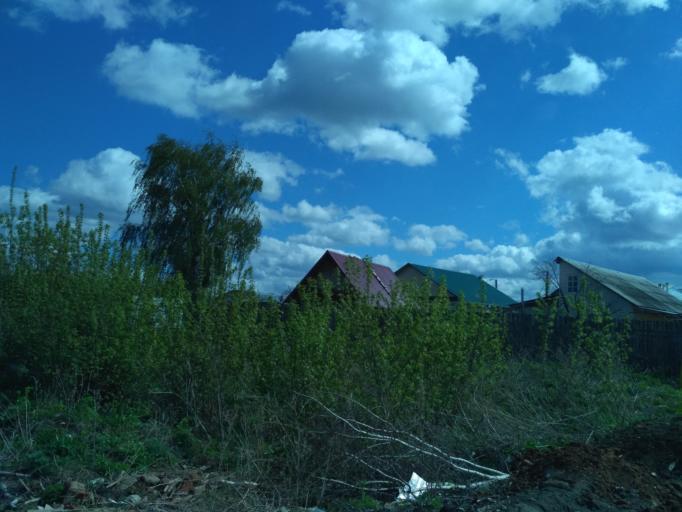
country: RU
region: Nizjnij Novgorod
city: Vad
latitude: 55.5303
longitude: 44.2104
